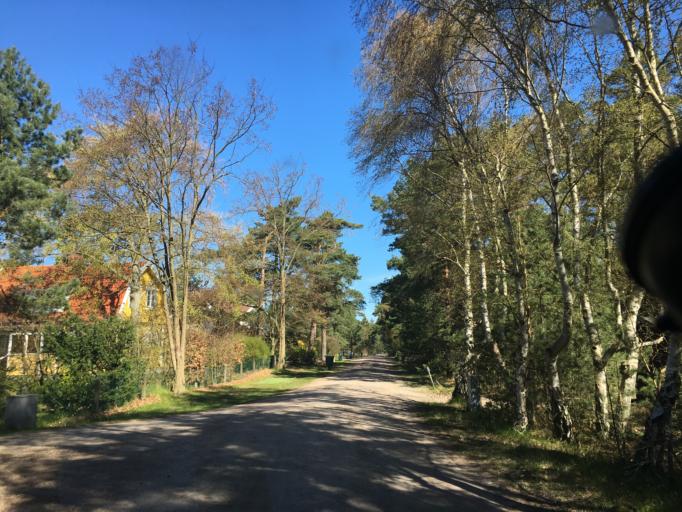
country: SE
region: Skane
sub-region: Vellinge Kommun
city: Ljunghusen
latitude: 55.3971
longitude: 12.9283
